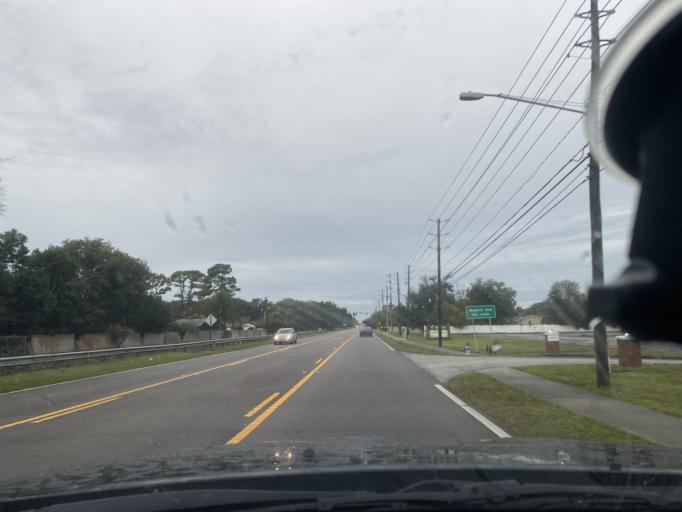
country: US
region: Florida
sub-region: Orange County
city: Union Park
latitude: 28.5392
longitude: -81.2636
